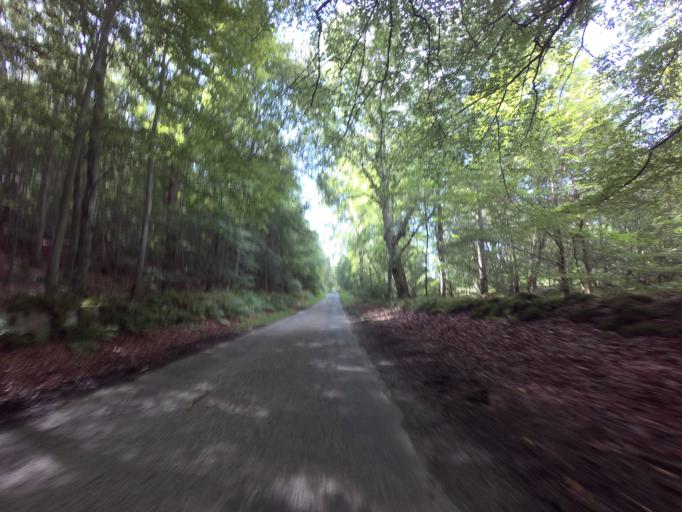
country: GB
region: Scotland
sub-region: Highland
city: Nairn
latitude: 57.5471
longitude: -3.8609
